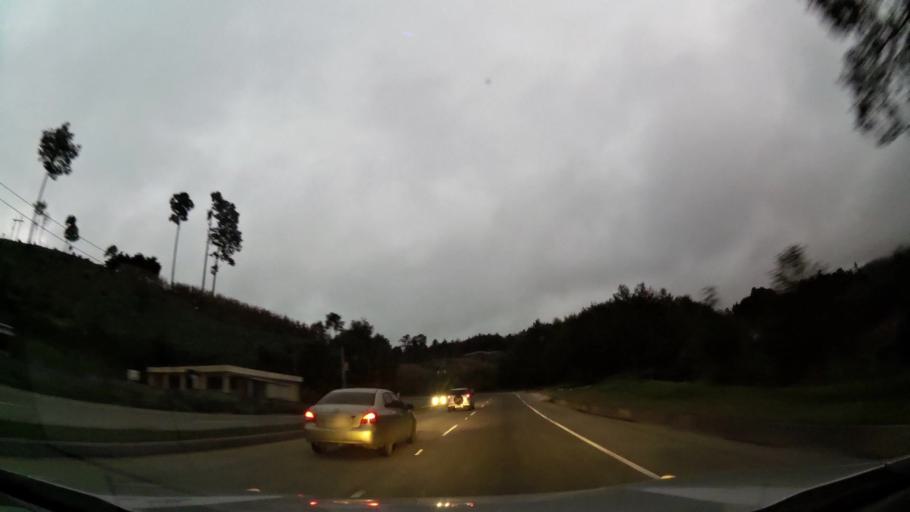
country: GT
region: Chimaltenango
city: Santa Apolonia
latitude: 14.8263
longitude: -91.0118
